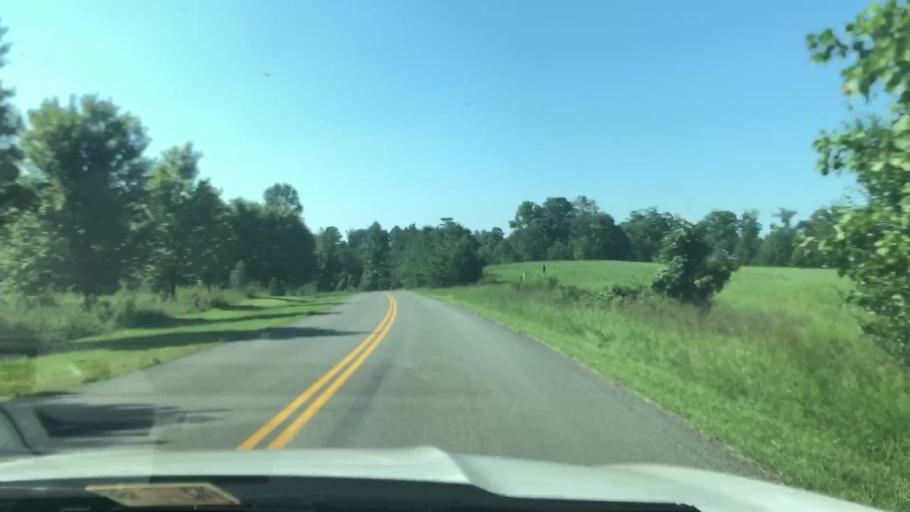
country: US
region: Virginia
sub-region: New Kent County
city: New Kent
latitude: 37.4714
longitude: -76.9295
